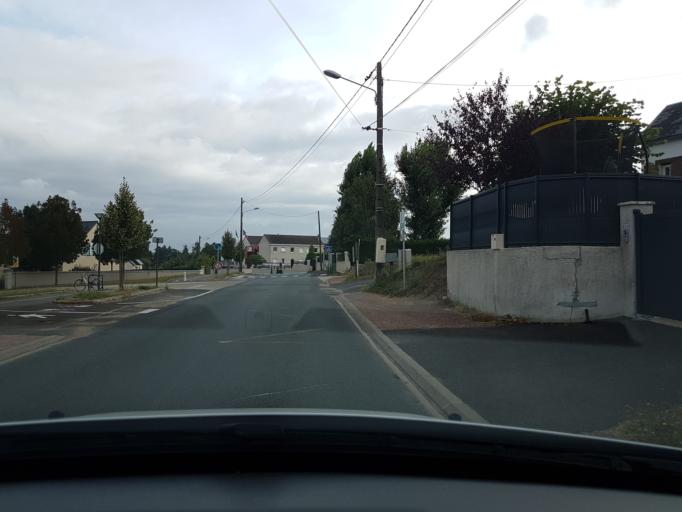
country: FR
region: Centre
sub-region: Departement d'Indre-et-Loire
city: Azay-sur-Cher
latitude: 47.3455
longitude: 0.8344
